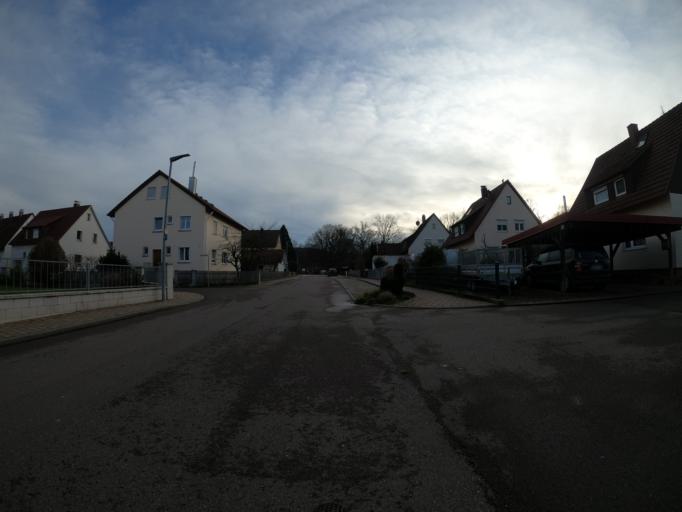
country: DE
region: Baden-Wuerttemberg
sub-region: Regierungsbezirk Stuttgart
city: Heiningen
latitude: 48.6592
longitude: 9.6456
